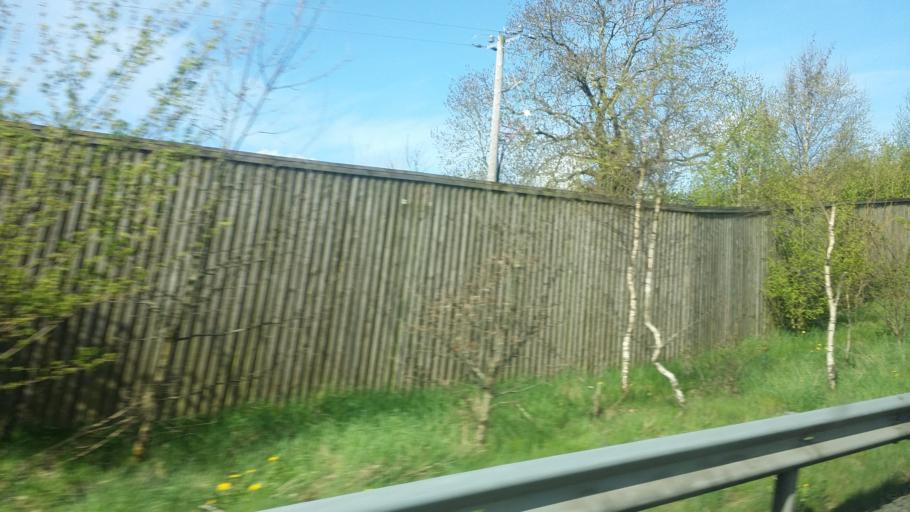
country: IE
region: Leinster
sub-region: An Mhi
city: Kells
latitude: 53.7305
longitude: -6.9553
